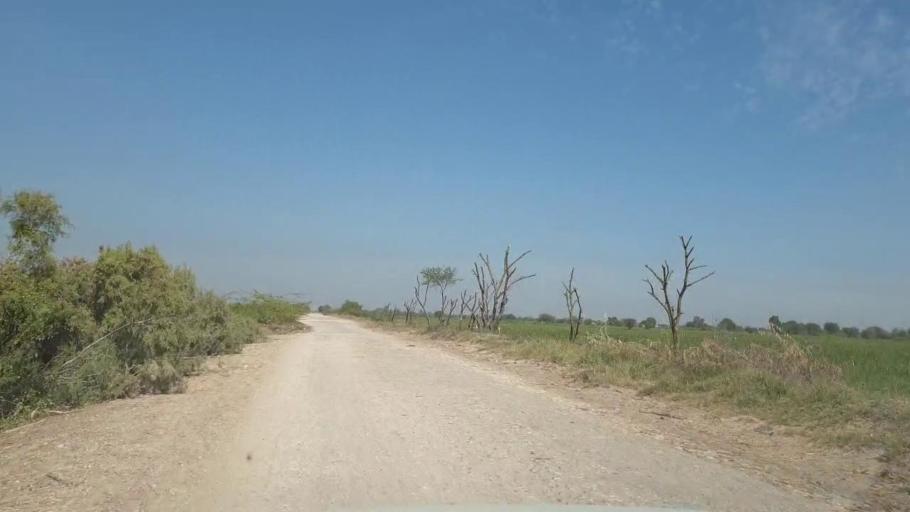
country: PK
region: Sindh
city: Mirpur Khas
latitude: 25.5909
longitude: 69.2010
